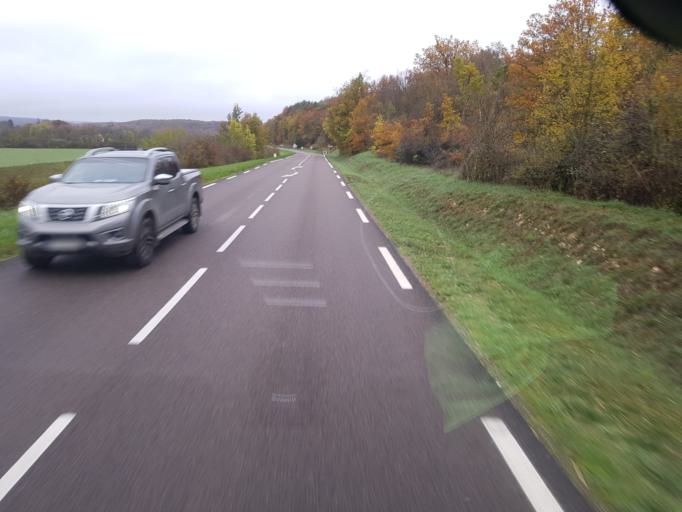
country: FR
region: Bourgogne
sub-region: Departement de la Cote-d'Or
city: Is-sur-Tille
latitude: 47.5298
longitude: 4.9938
